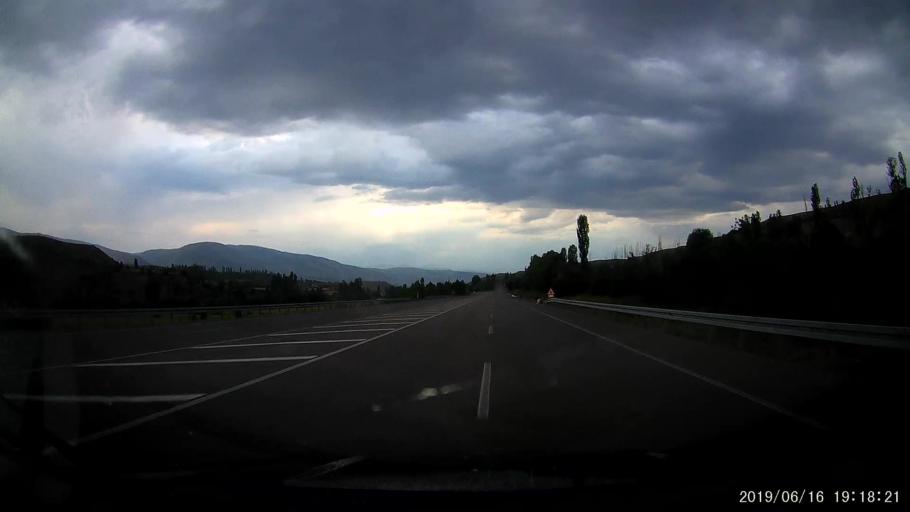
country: TR
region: Sivas
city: Akincilar
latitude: 40.0951
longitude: 38.4606
